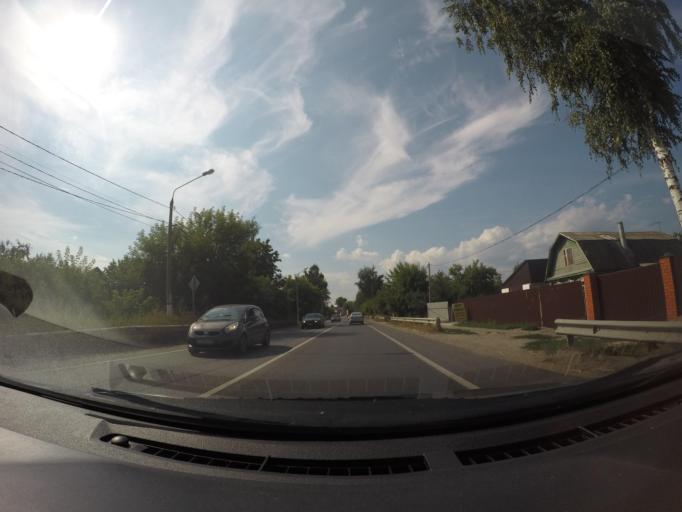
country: RU
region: Moskovskaya
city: Rechitsy
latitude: 55.5978
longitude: 38.4666
